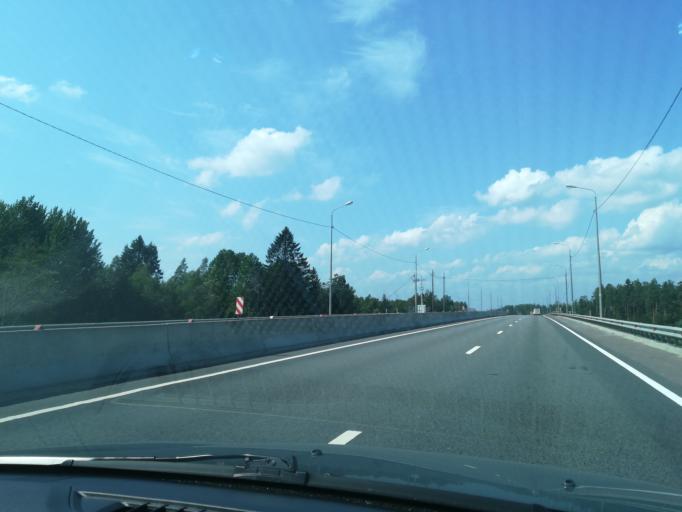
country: RU
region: Leningrad
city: Kingisepp
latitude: 59.5966
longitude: 28.7267
